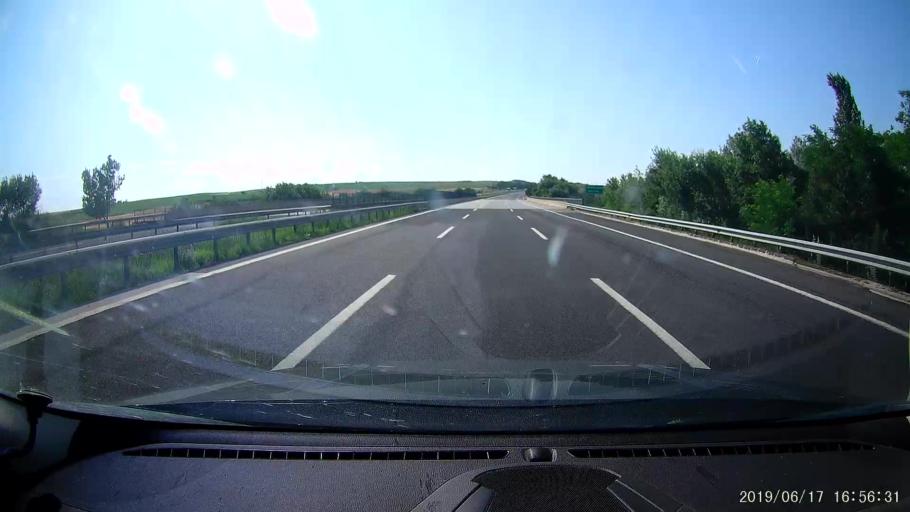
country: TR
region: Edirne
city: Haskoy
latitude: 41.5876
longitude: 26.9346
